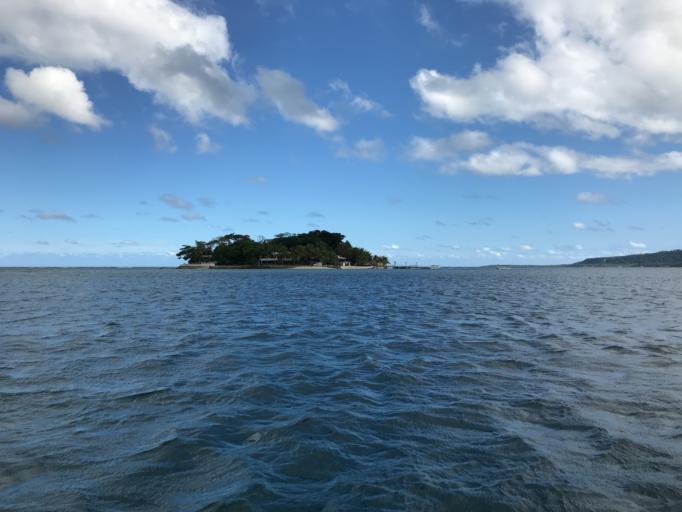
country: VU
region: Shefa
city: Port-Vila
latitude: -17.6941
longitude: 168.2655
